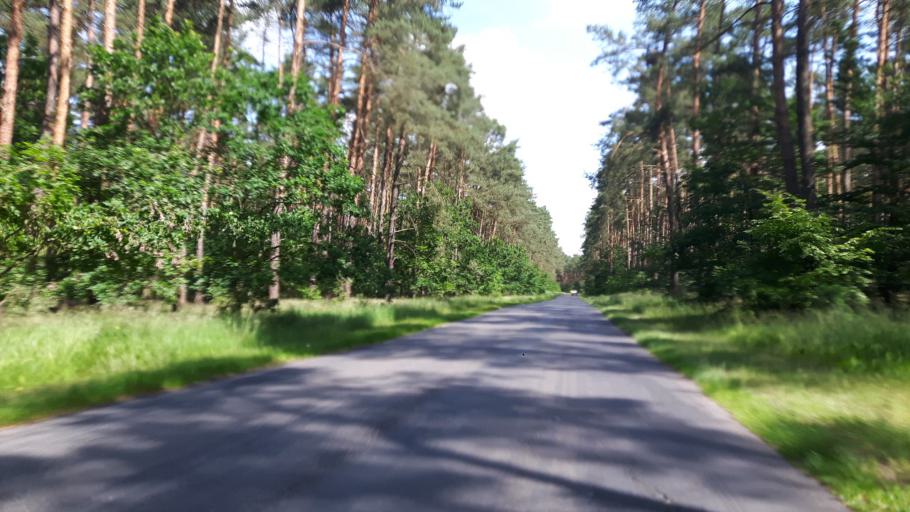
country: PL
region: West Pomeranian Voivodeship
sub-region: Powiat goleniowski
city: Goleniow
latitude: 53.5101
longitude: 14.7871
